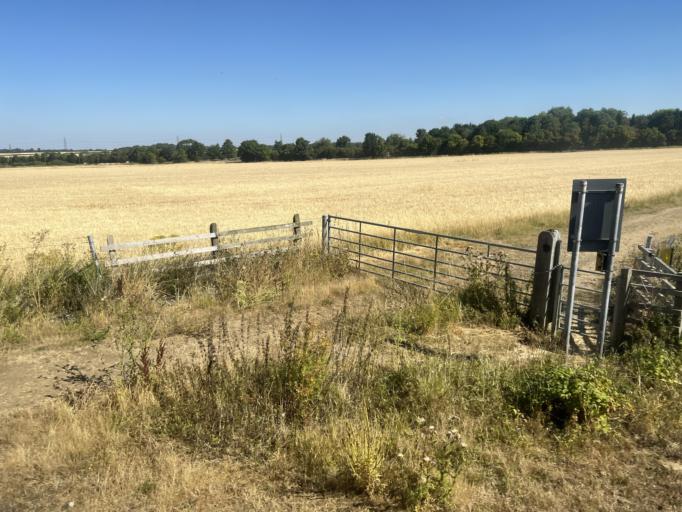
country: GB
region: England
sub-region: Lincolnshire
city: Heckington
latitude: 52.9821
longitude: -0.3192
